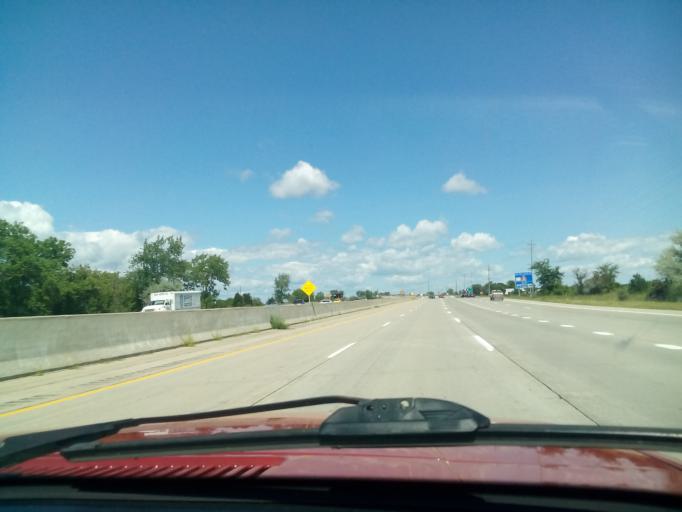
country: US
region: Michigan
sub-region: Bay County
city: Bay City
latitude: 43.6100
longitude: -83.9476
